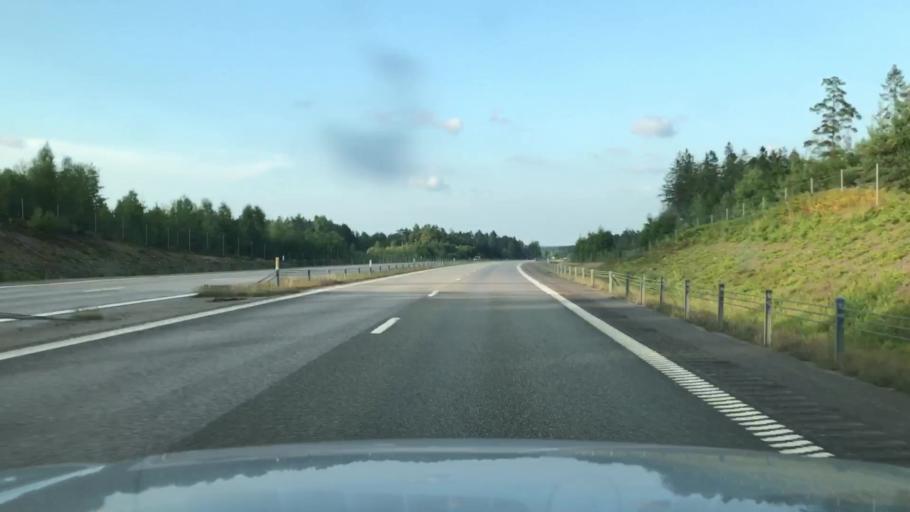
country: SE
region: Kronoberg
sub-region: Markaryds Kommun
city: Markaryd
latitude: 56.4273
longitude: 13.5604
